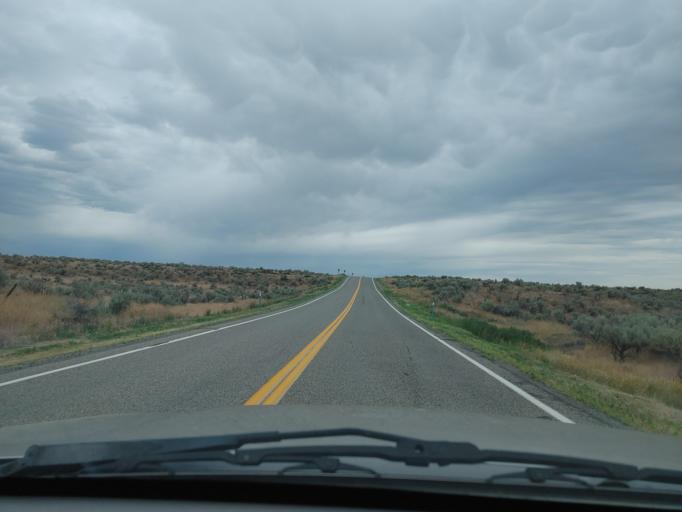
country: US
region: Idaho
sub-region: Lincoln County
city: Shoshone
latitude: 43.0804
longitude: -114.1011
